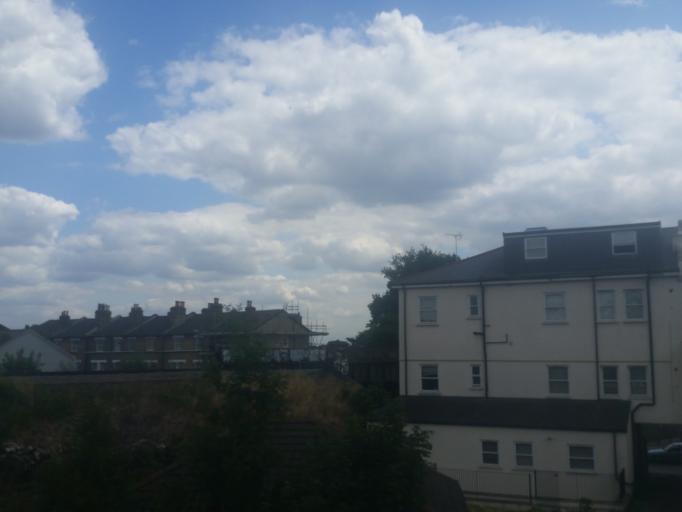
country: GB
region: England
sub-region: Greater London
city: Thornton Heath
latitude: 51.4039
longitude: -0.0696
